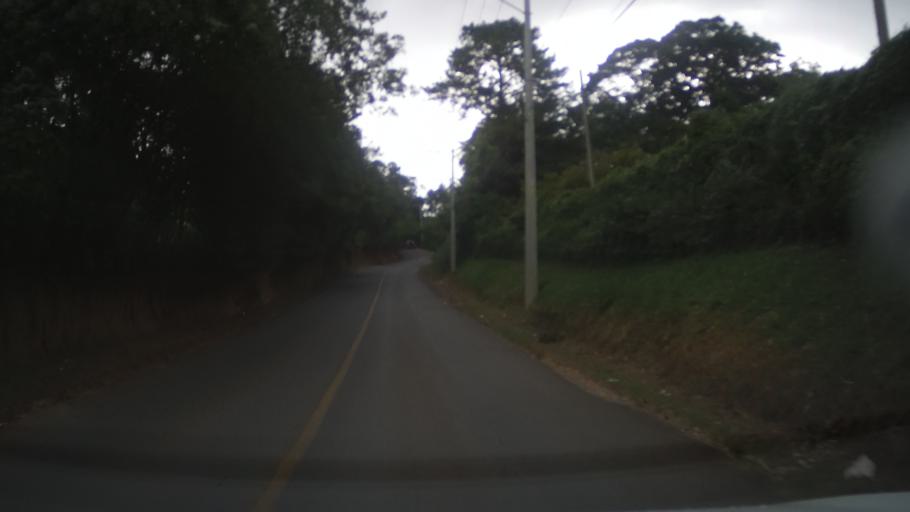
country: BR
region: Sao Paulo
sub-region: Itupeva
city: Itupeva
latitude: -23.1908
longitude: -47.0276
